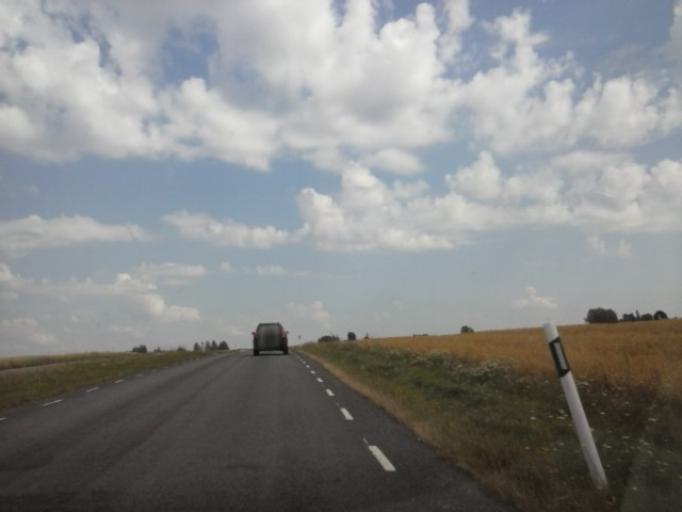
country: EE
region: Jogevamaa
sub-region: Tabivere vald
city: Tabivere
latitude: 58.5092
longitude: 26.6817
